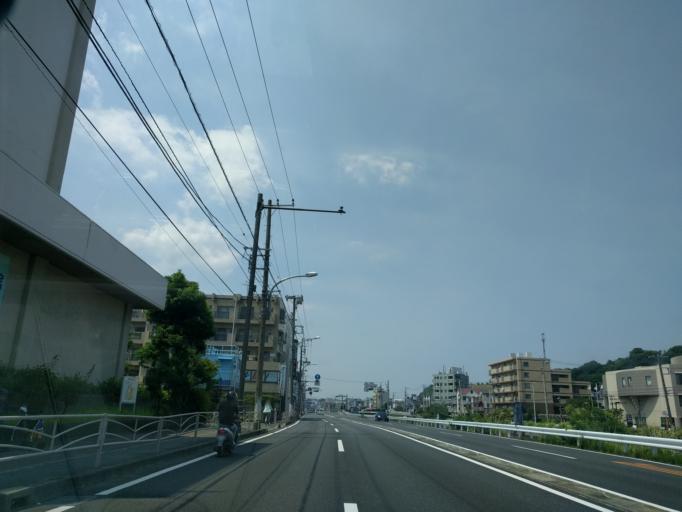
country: JP
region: Kanagawa
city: Yokohama
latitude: 35.4204
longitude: 139.6254
